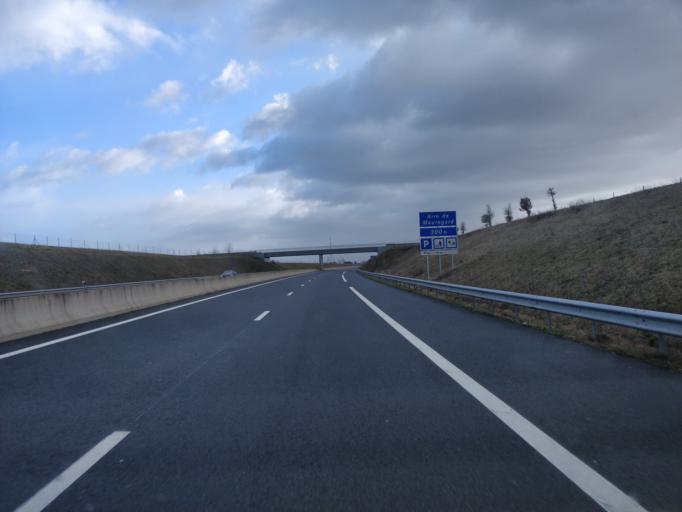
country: FR
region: Centre
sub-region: Departement du Loiret
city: Puiseaux
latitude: 48.0985
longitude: 2.0624
